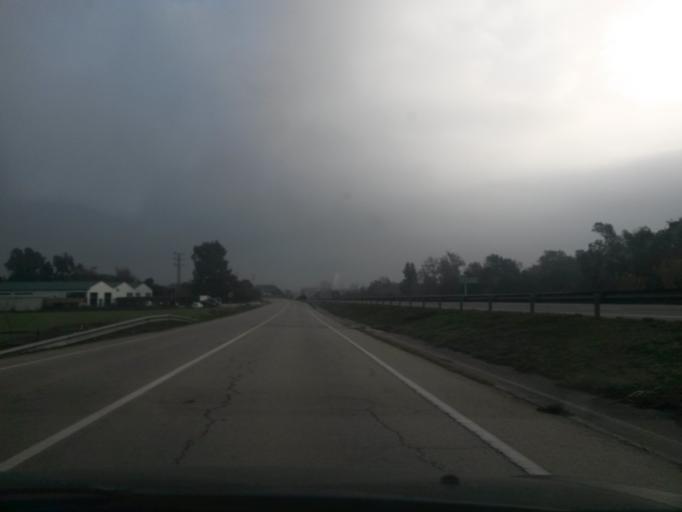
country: ES
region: Catalonia
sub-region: Provincia de Girona
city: Llagostera
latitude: 41.8301
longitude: 2.9159
